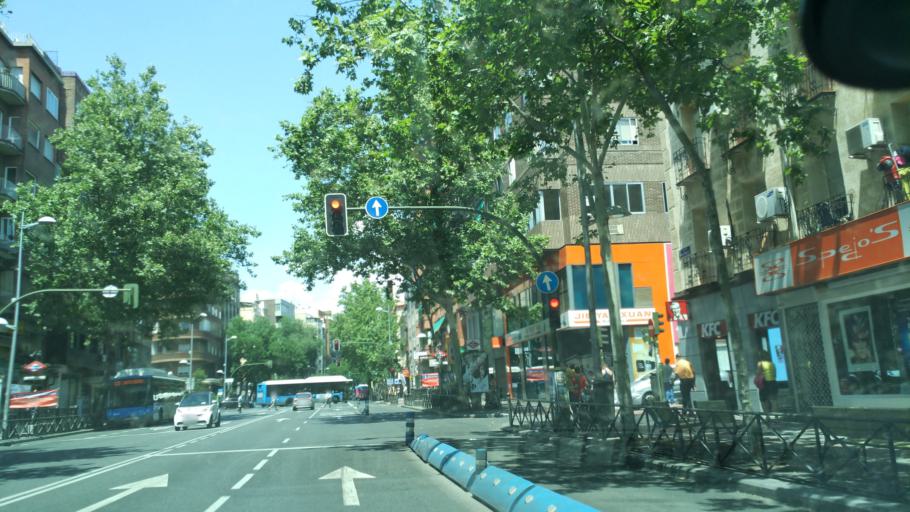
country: ES
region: Madrid
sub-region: Provincia de Madrid
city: Tetuan de las Victorias
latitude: 40.4533
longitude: -3.7030
